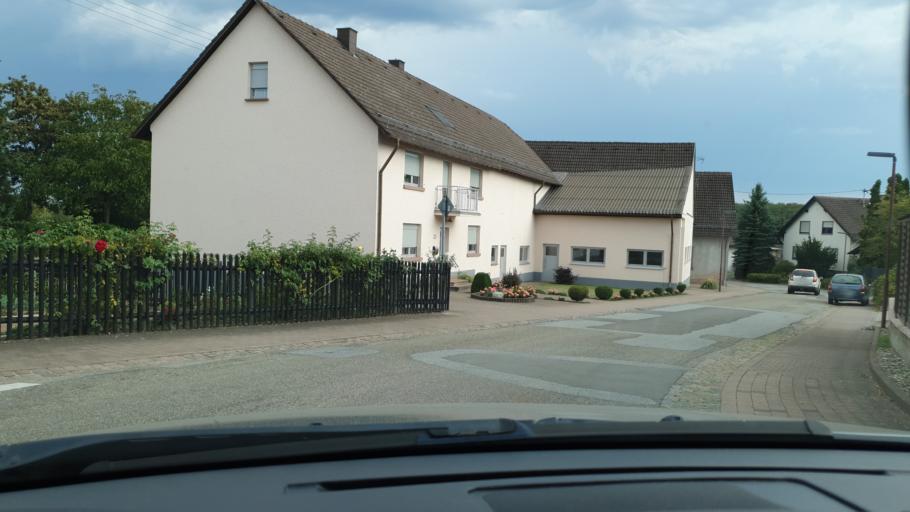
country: DE
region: Rheinland-Pfalz
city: Knopp-Labach
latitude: 49.3338
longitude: 7.5062
